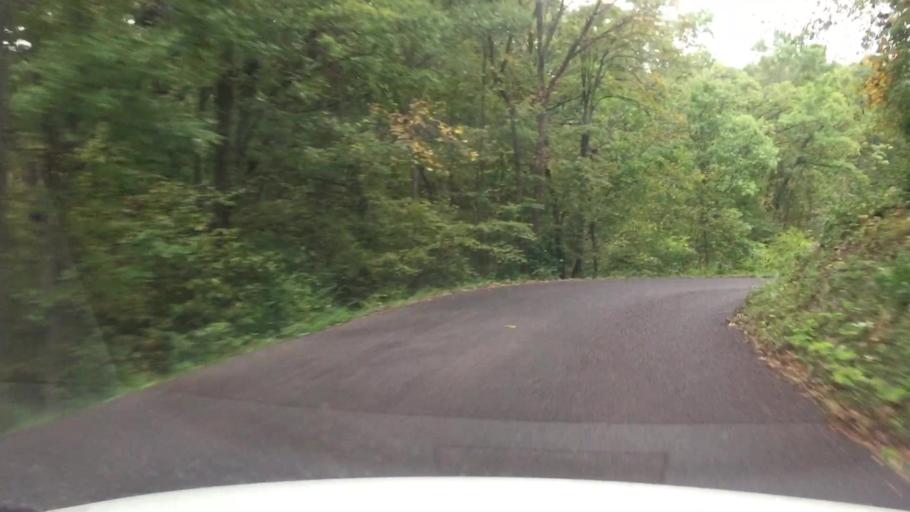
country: US
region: Missouri
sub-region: Boone County
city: Ashland
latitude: 38.8137
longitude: -92.2780
